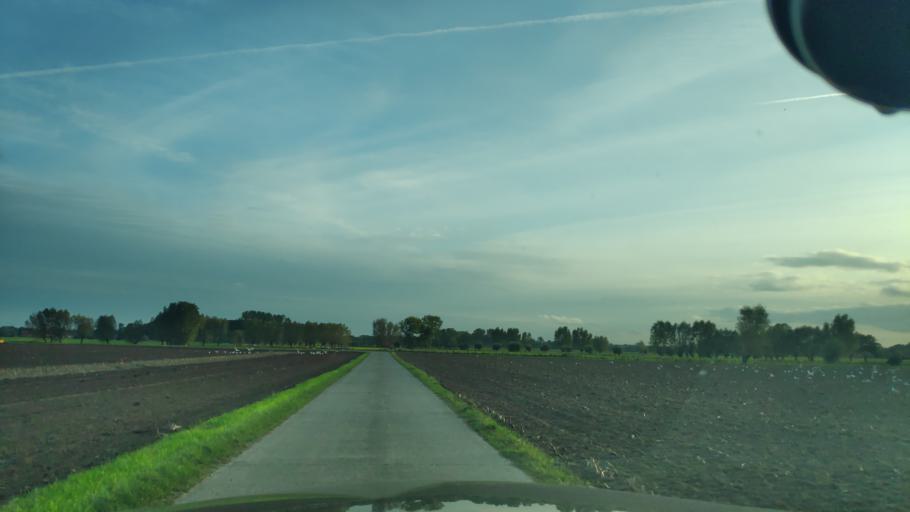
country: BE
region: Flanders
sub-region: Provincie Oost-Vlaanderen
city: Aalter
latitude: 51.1122
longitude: 3.4905
